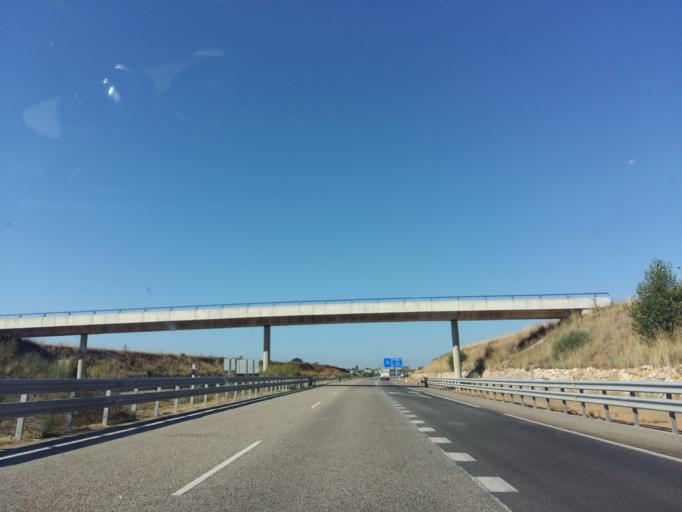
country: ES
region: Castille and Leon
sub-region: Provincia de Leon
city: San Andres del Rabanedo
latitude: 42.5740
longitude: -5.6312
